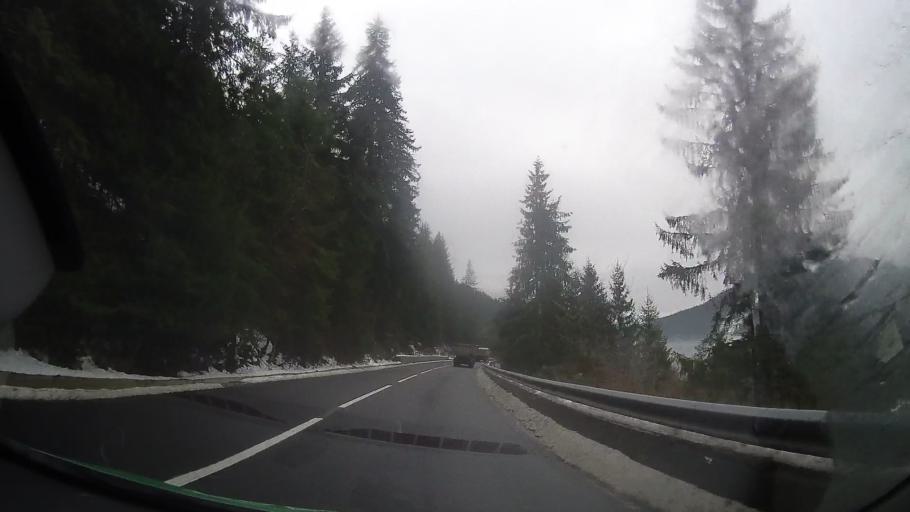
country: RO
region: Harghita
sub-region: Municipiul Gheorgheni
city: Gheorgheni
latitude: 46.7718
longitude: 25.7115
